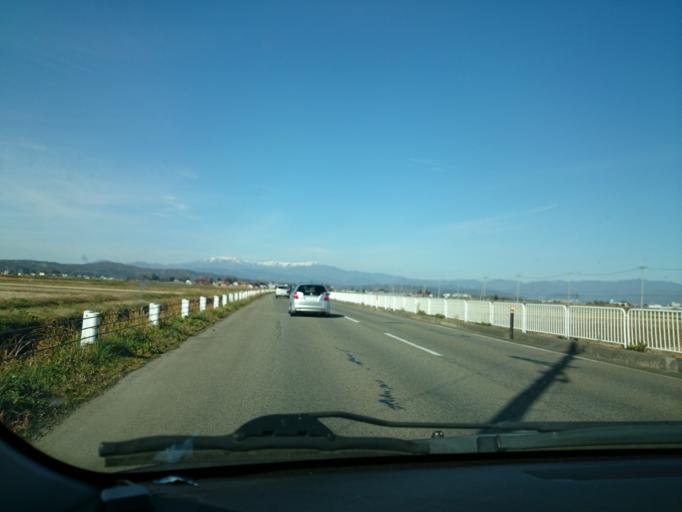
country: JP
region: Fukushima
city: Kitakata
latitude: 37.5389
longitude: 139.8337
